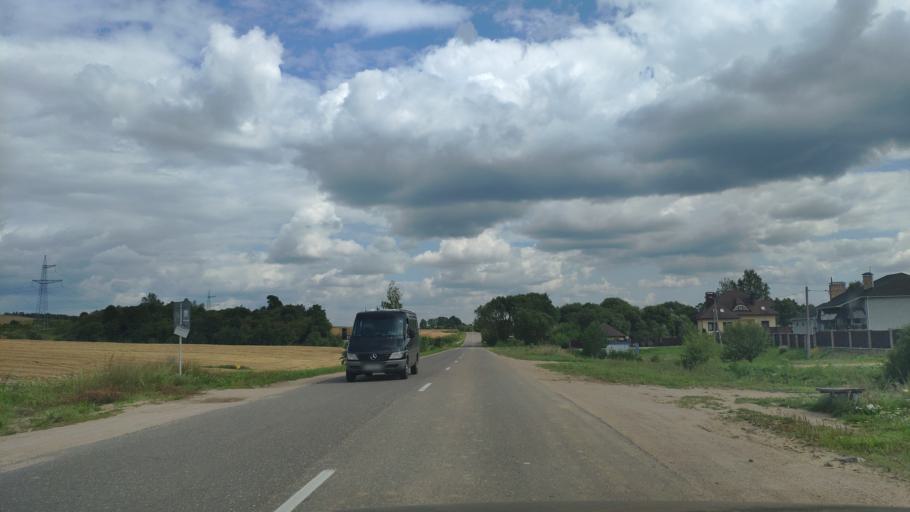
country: BY
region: Minsk
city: Khatsyezhyna
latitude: 53.8714
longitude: 27.3085
